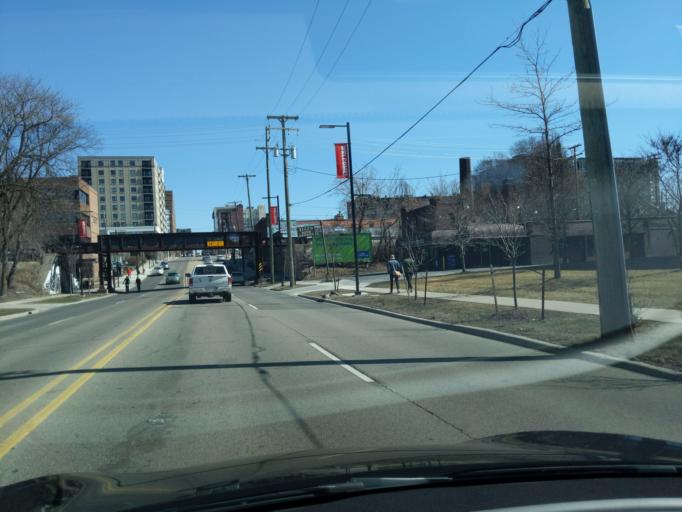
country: US
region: Michigan
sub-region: Washtenaw County
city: Ann Arbor
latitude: 42.2816
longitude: -83.7529
